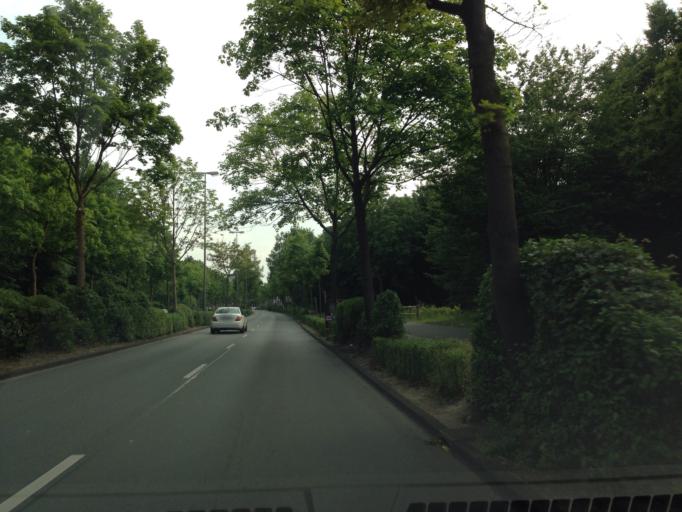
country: DE
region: North Rhine-Westphalia
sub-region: Regierungsbezirk Munster
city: Muenster
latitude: 51.9723
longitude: 7.6049
